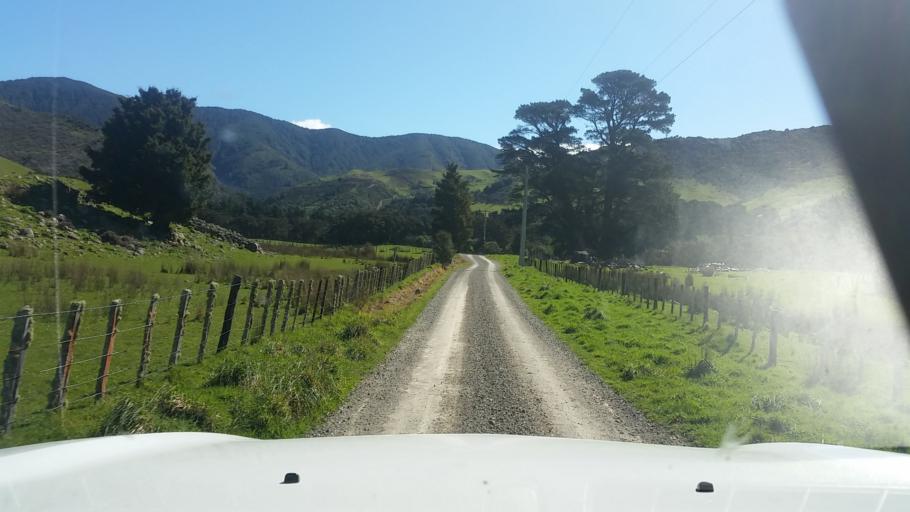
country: NZ
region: Wellington
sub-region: Masterton District
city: Masterton
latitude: -40.8854
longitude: 175.5141
